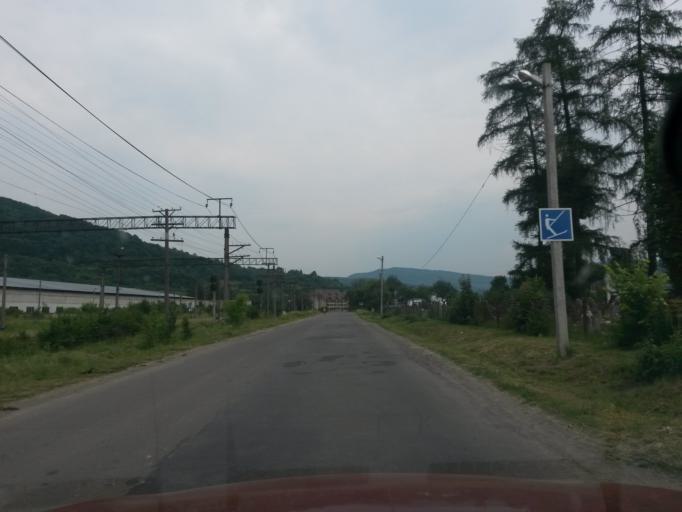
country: UA
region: Zakarpattia
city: Velykyi Bereznyi
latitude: 48.9044
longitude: 22.4585
